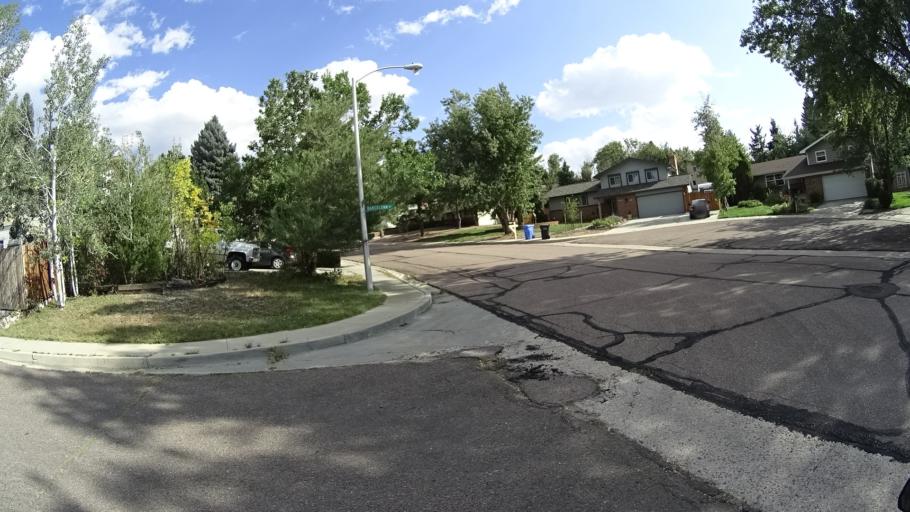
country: US
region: Colorado
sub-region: El Paso County
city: Cimarron Hills
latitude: 38.8731
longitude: -104.7361
